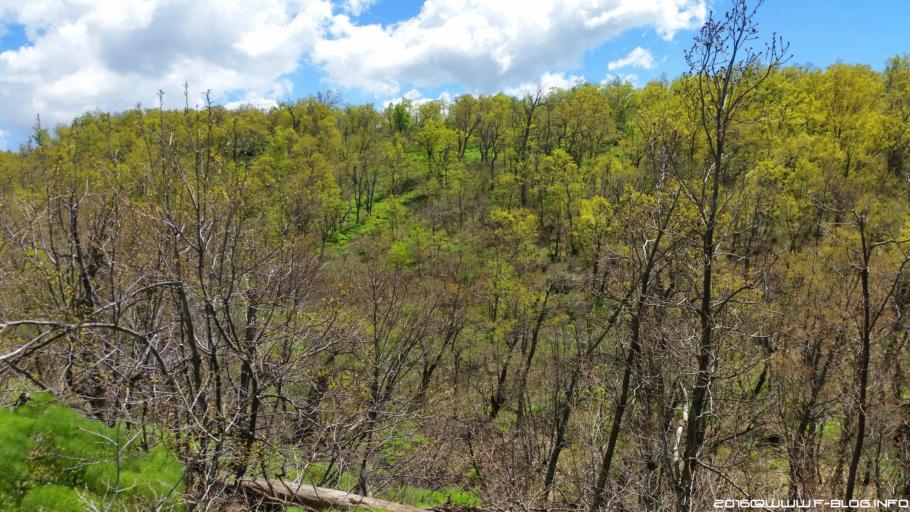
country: IQ
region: Arbil
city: Mergasur
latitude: 37.1243
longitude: 44.2990
